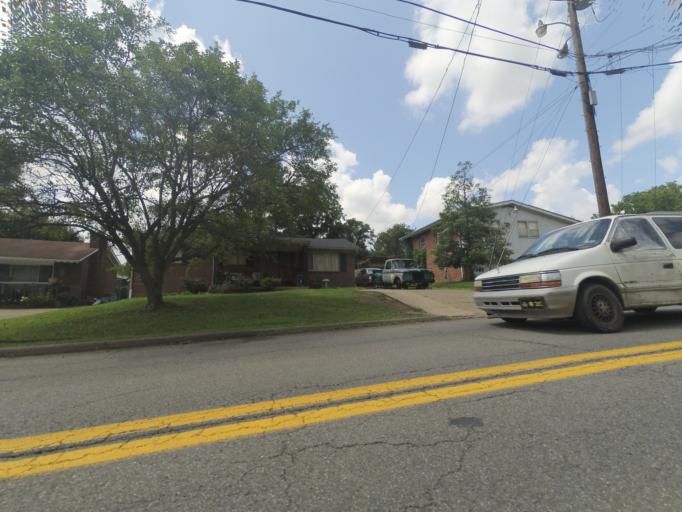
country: US
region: West Virginia
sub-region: Cabell County
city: Pea Ridge
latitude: 38.4039
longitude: -82.3801
